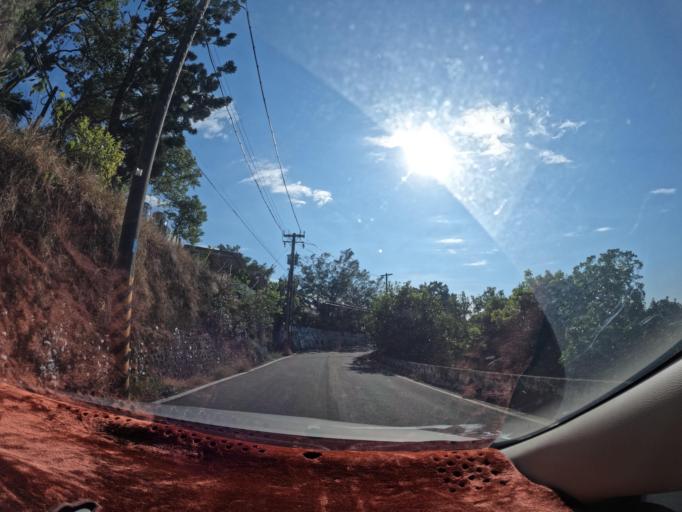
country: TW
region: Taiwan
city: Yujing
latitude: 23.0270
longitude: 120.3853
